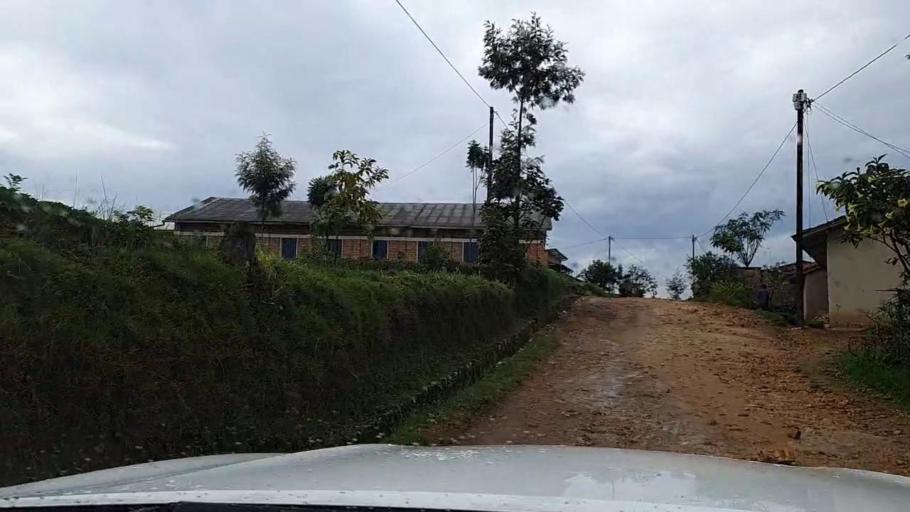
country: RW
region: Southern Province
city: Nzega
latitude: -2.4591
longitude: 29.4670
